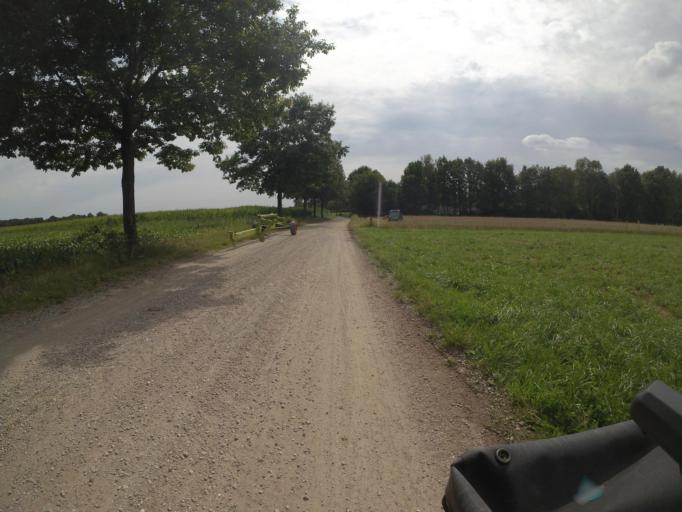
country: NL
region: North Brabant
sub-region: Gemeente Valkenswaard
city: Valkenswaard
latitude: 51.3023
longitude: 5.4257
